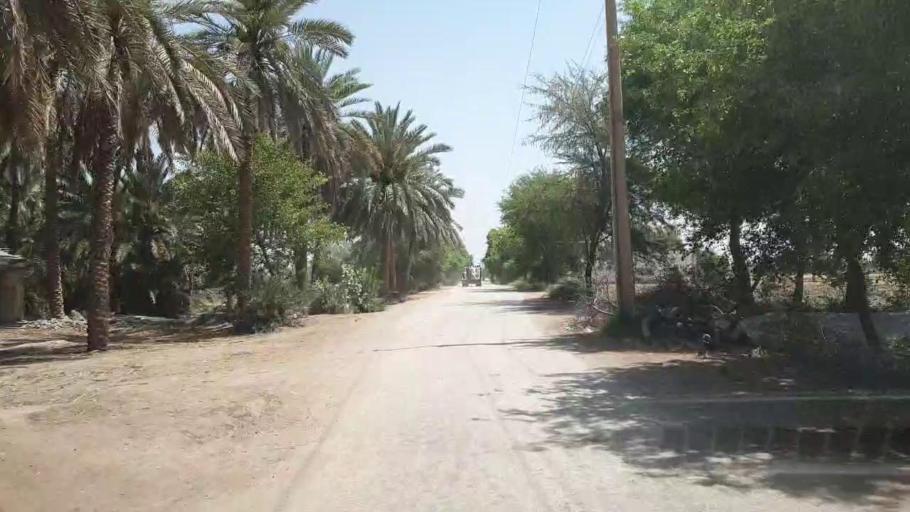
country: PK
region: Sindh
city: Adilpur
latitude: 27.8277
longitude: 69.2510
